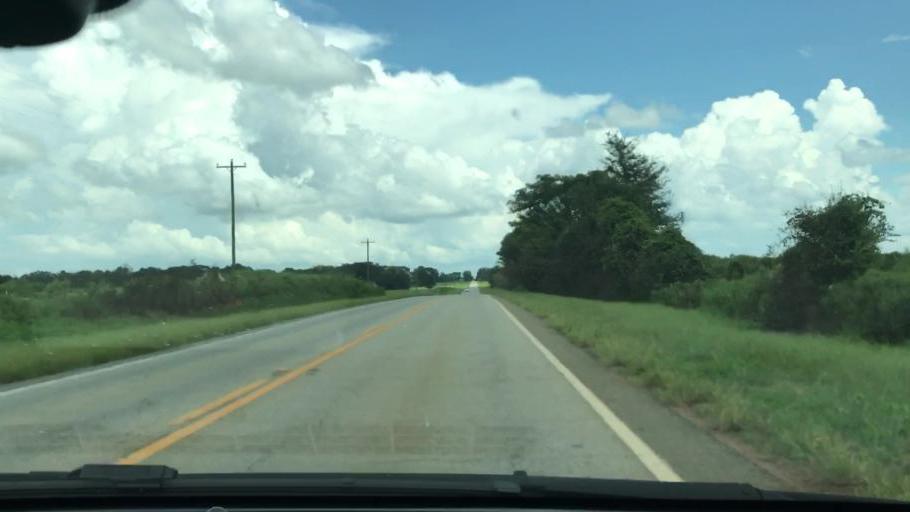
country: US
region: Georgia
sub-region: Seminole County
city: Donalsonville
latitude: 30.9795
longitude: -84.9927
